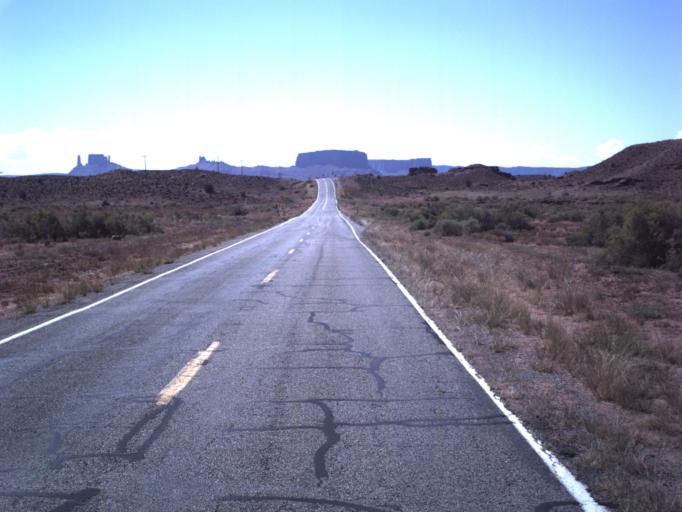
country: US
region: Utah
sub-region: Grand County
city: Moab
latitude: 38.7573
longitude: -109.3255
